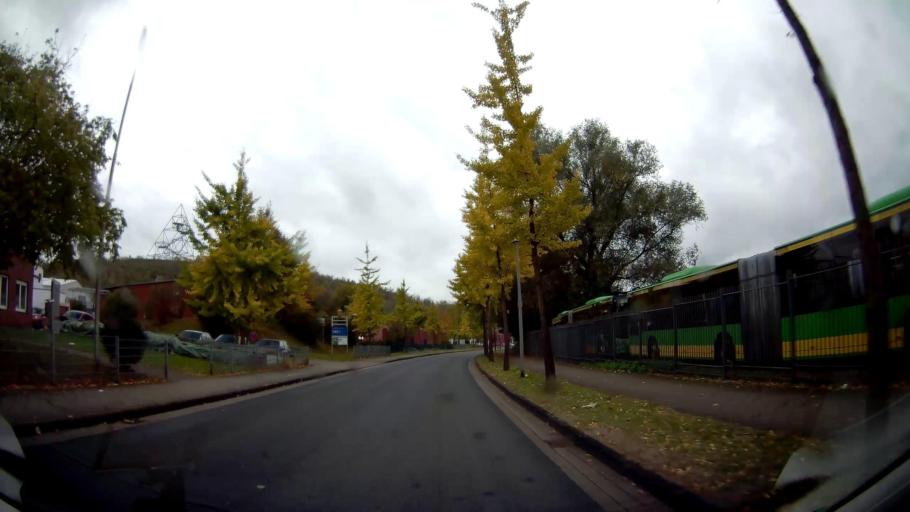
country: DE
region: North Rhine-Westphalia
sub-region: Regierungsbezirk Munster
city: Bottrop
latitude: 51.5314
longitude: 6.9570
